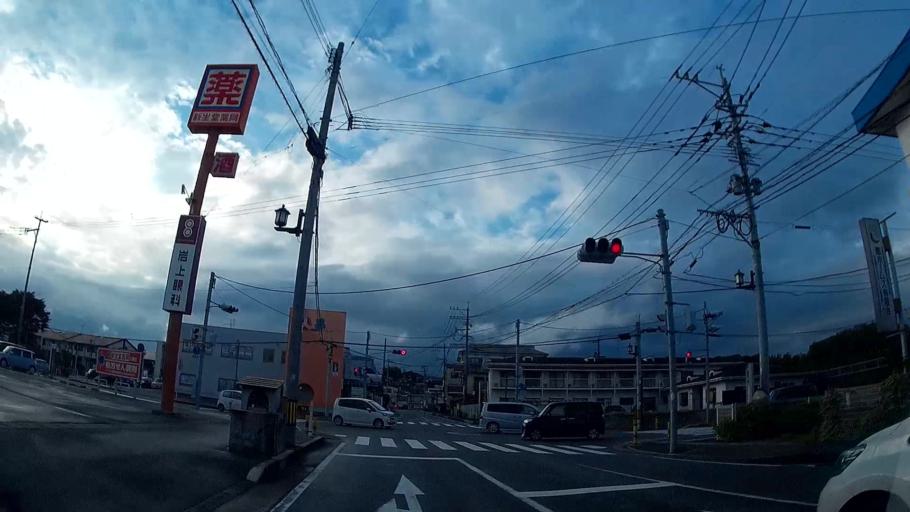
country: JP
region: Kumamoto
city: Ozu
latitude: 32.8761
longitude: 130.8702
